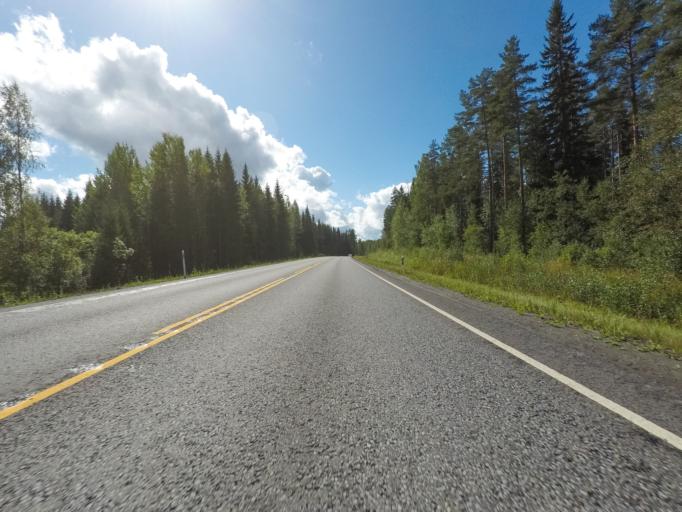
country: FI
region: Central Finland
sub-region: Jyvaeskylae
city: Hankasalmi
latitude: 62.3366
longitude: 26.5378
